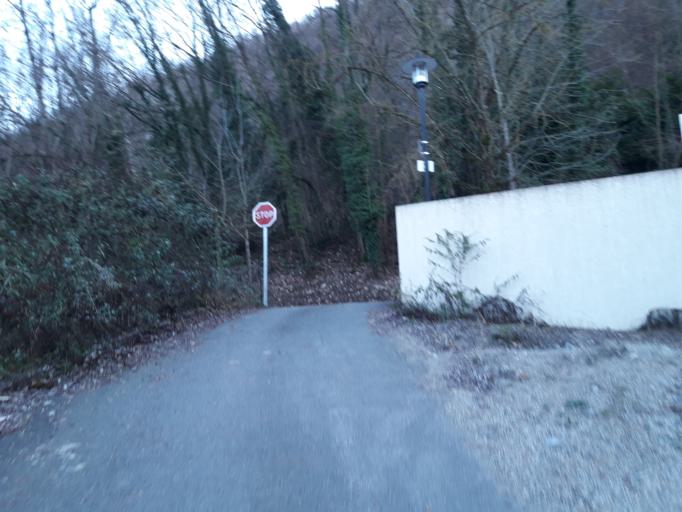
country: FR
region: Rhone-Alpes
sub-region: Departement de l'Isere
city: Gieres
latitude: 45.1783
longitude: 5.7825
